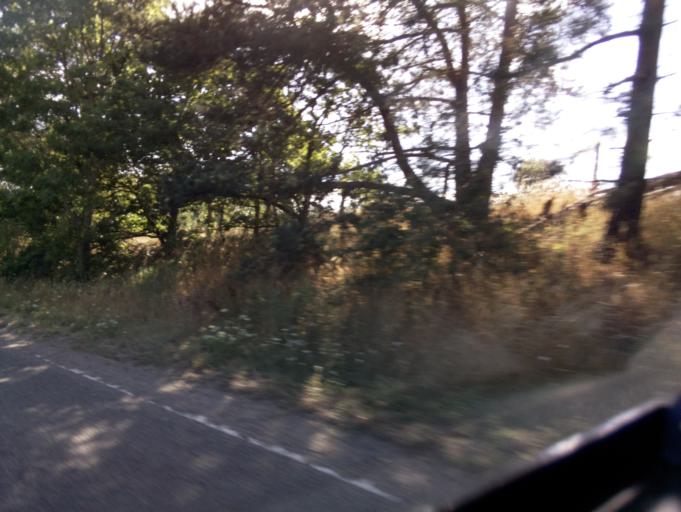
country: GB
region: England
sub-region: Hampshire
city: Romsey
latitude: 50.9556
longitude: -1.5328
